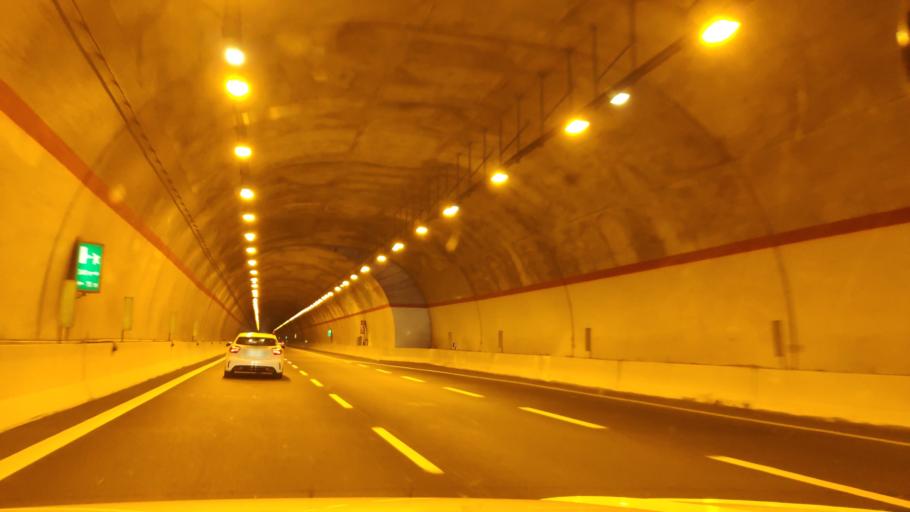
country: IT
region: Calabria
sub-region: Provincia di Cosenza
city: Mormanno
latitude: 39.9009
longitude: 15.9730
